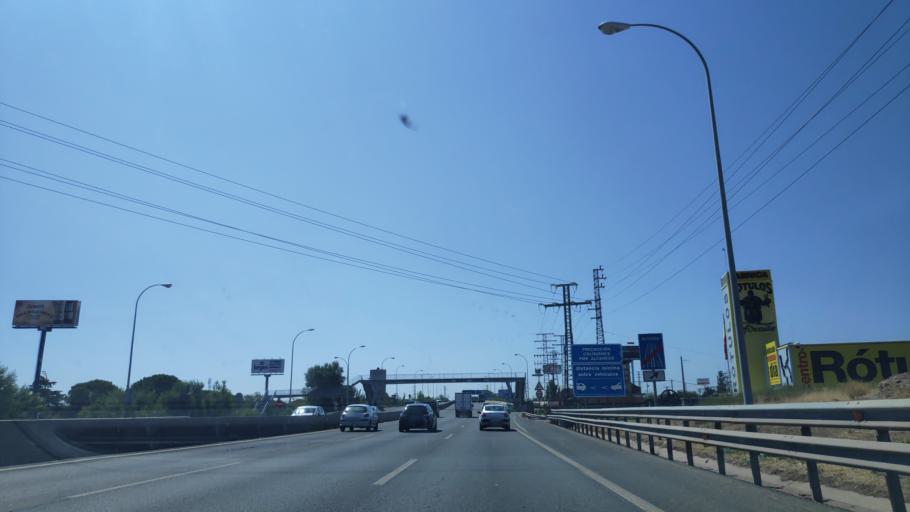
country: ES
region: Madrid
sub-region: Provincia de Madrid
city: Villaverde
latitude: 40.3459
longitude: -3.7235
